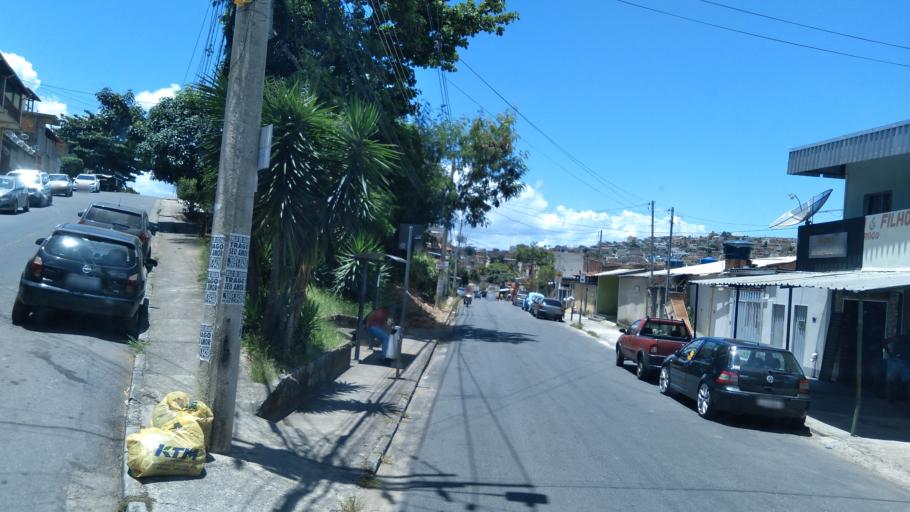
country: BR
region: Minas Gerais
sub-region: Santa Luzia
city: Santa Luzia
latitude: -19.8363
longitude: -43.8912
